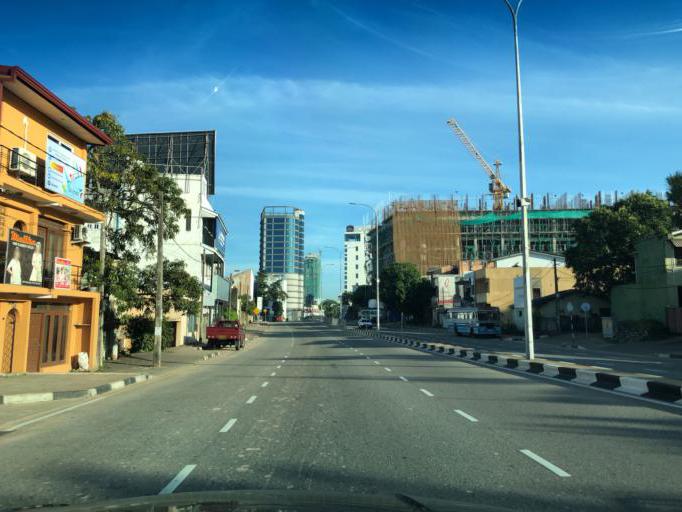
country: LK
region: Western
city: Pita Kotte
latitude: 6.8814
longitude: 79.8762
